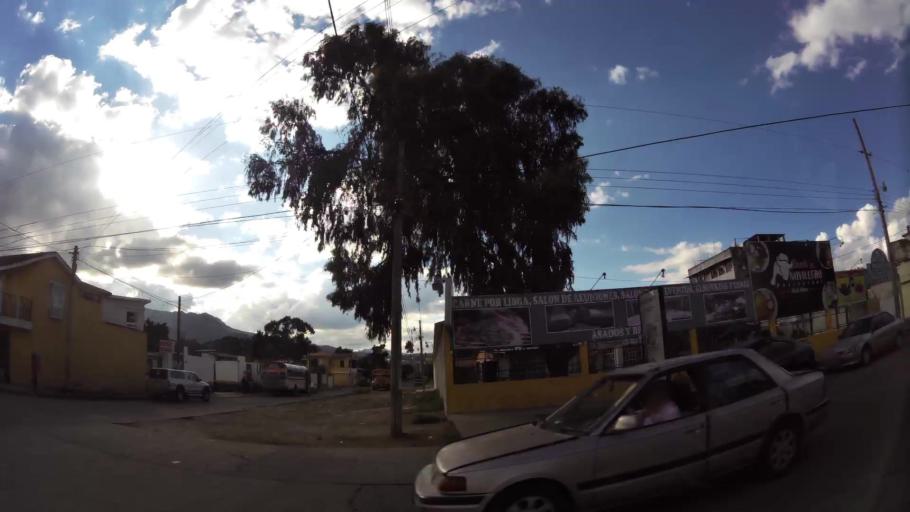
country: GT
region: Quetzaltenango
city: Quetzaltenango
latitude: 14.8491
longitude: -91.5285
